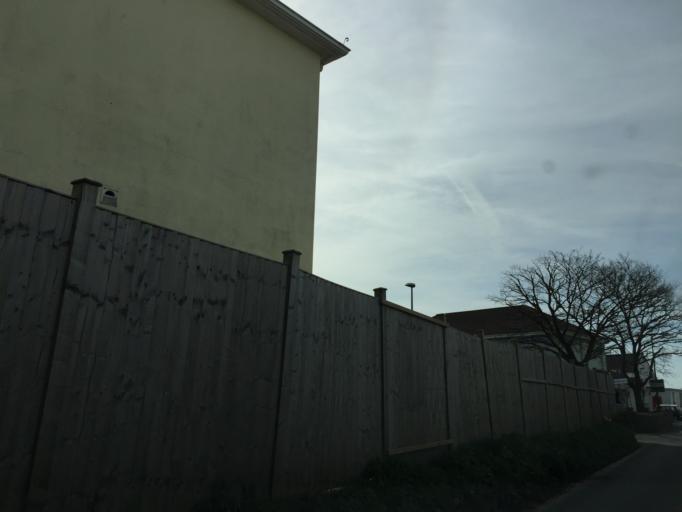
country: JE
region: St Helier
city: Saint Helier
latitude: 49.2191
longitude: -2.1404
